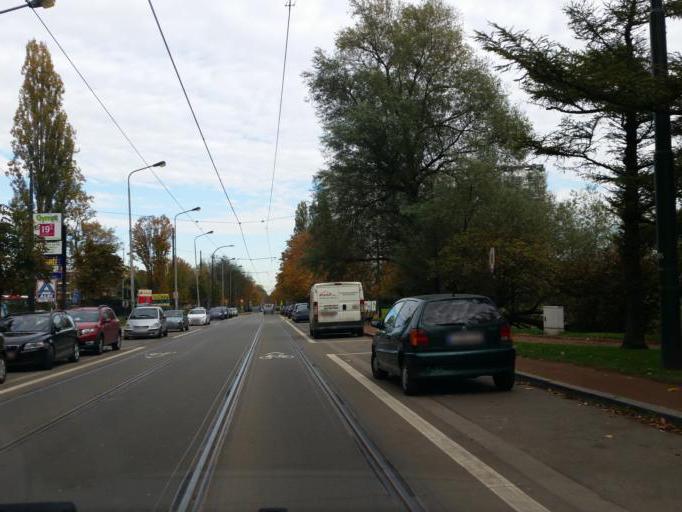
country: BE
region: Flanders
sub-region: Provincie Vlaams-Brabant
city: Dilbeek
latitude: 50.8264
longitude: 4.2867
